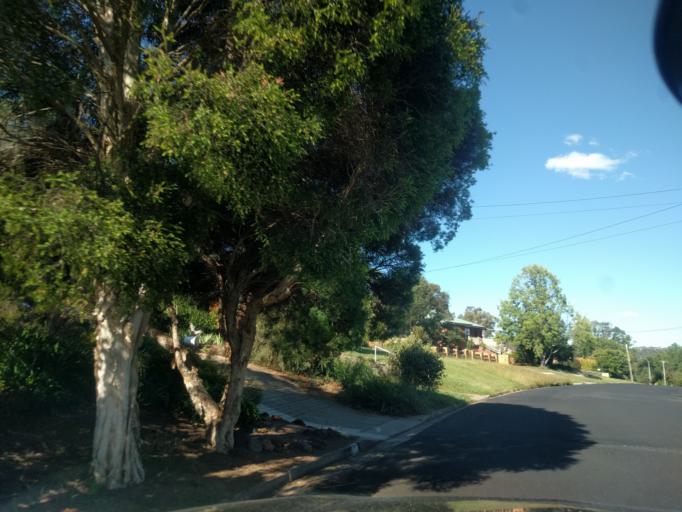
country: AU
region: New South Wales
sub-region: Armidale Dumaresq
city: Armidale
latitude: -30.4998
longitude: 151.6686
